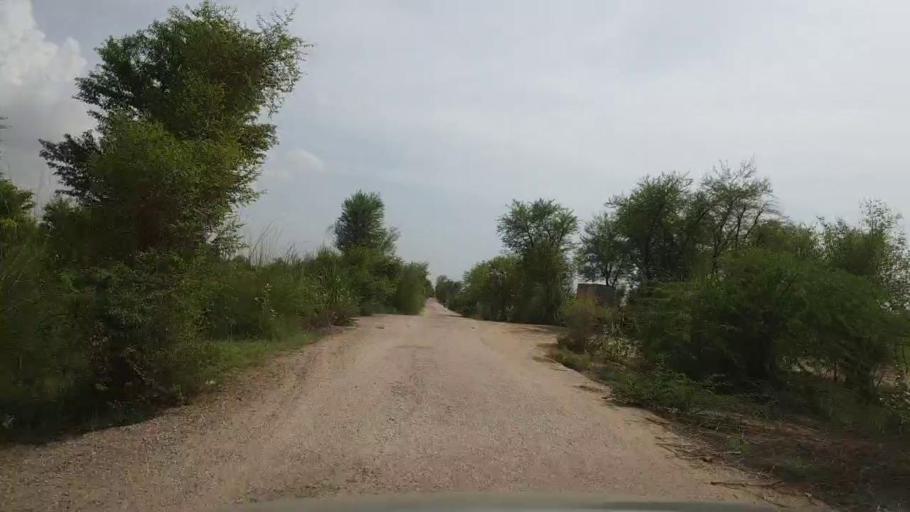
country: PK
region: Sindh
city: Kot Diji
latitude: 27.1093
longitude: 69.0219
